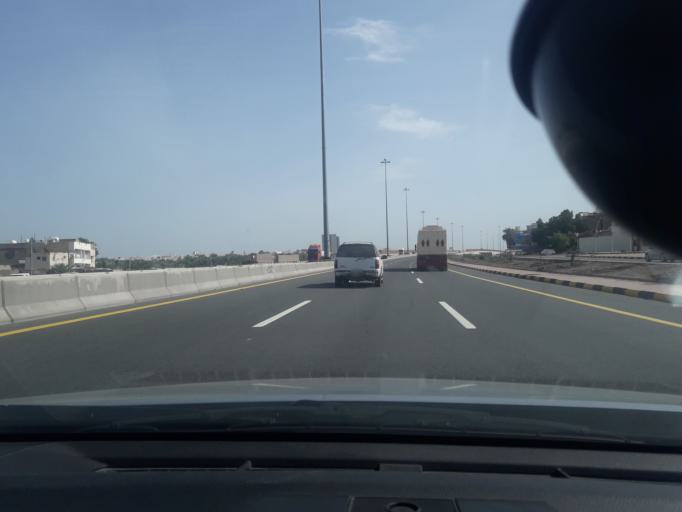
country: SA
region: Al Madinah al Munawwarah
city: Medina
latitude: 24.4432
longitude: 39.6353
